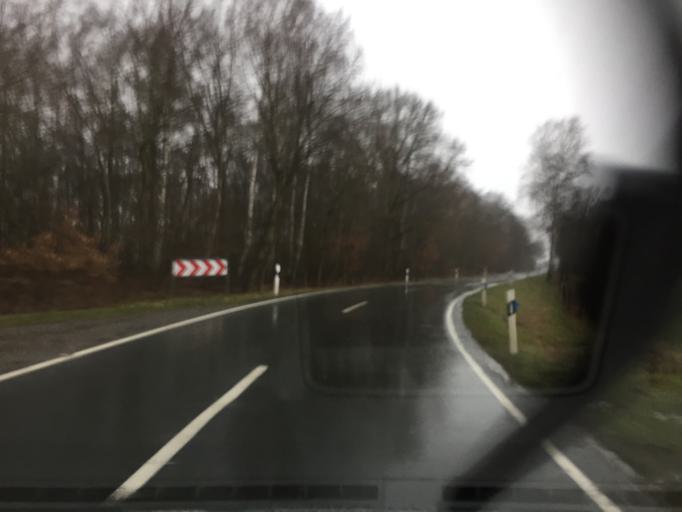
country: DE
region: Lower Saxony
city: Maasen
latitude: 52.6451
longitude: 8.8831
